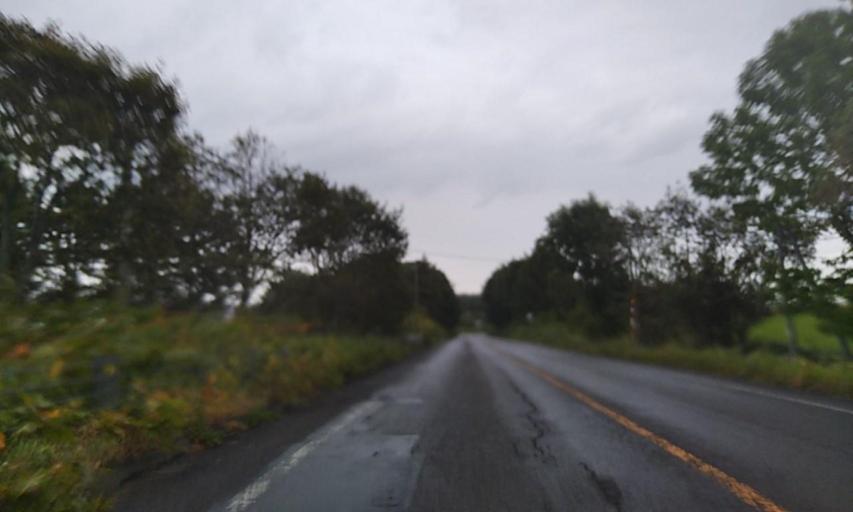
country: JP
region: Hokkaido
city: Mombetsu
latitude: 44.4824
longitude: 143.1000
